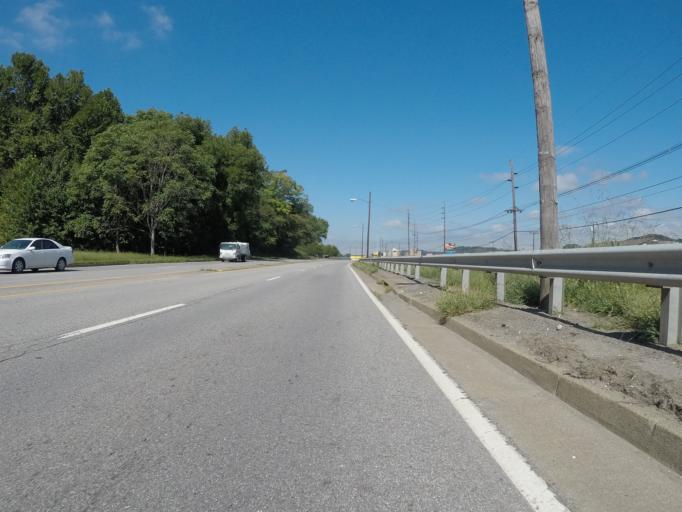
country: US
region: Kentucky
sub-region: Boyd County
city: Ashland
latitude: 38.4627
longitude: -82.6153
